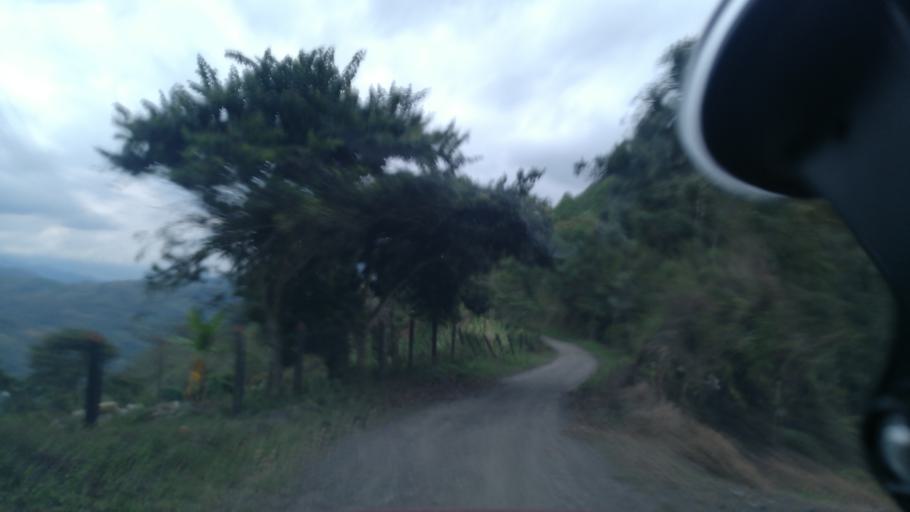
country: CO
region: Cundinamarca
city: Vergara
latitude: 5.1704
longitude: -74.2659
